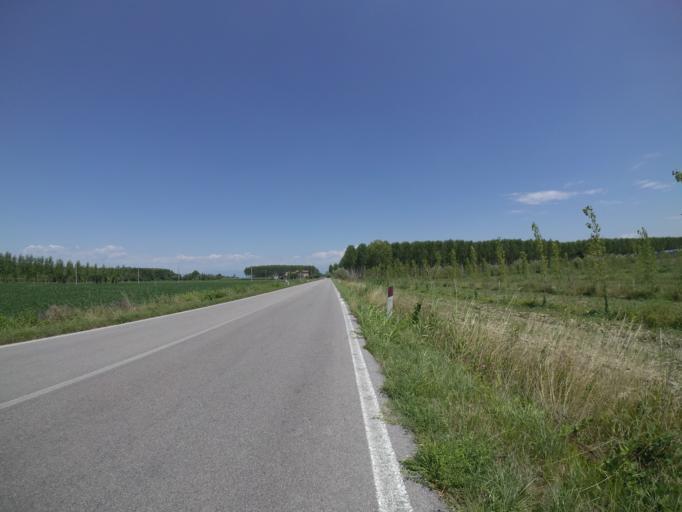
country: IT
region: Friuli Venezia Giulia
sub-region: Provincia di Udine
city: Talmassons
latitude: 45.8908
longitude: 13.1274
